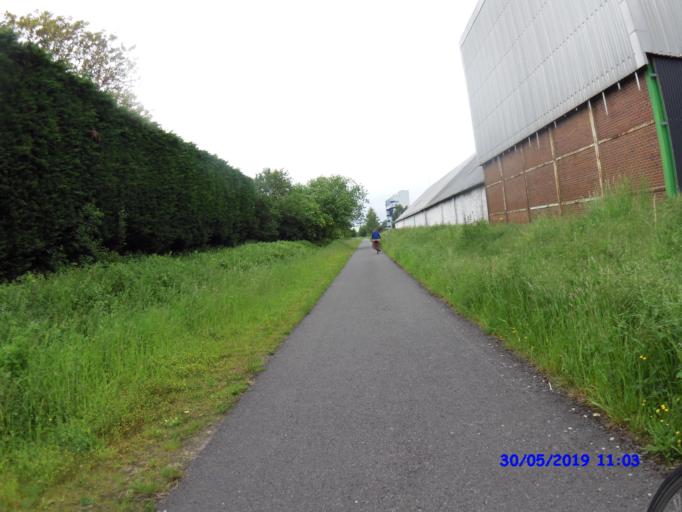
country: BE
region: Wallonia
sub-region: Province du Hainaut
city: Thuin
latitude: 50.2809
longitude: 4.3175
